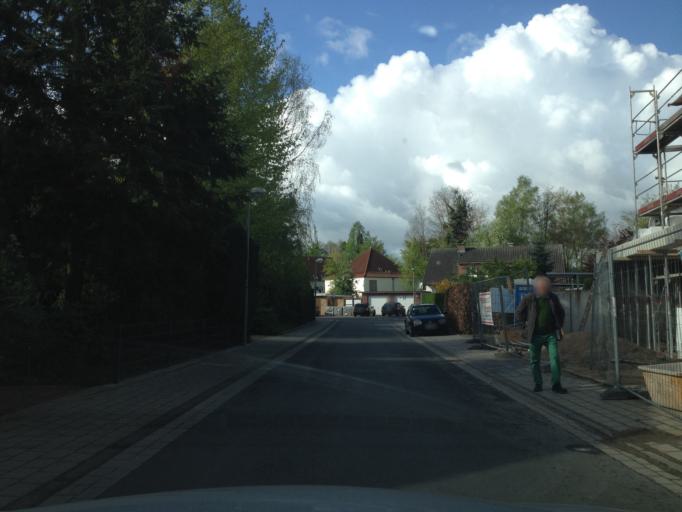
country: DE
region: North Rhine-Westphalia
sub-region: Regierungsbezirk Detmold
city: Guetersloh
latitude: 51.8852
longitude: 8.3984
